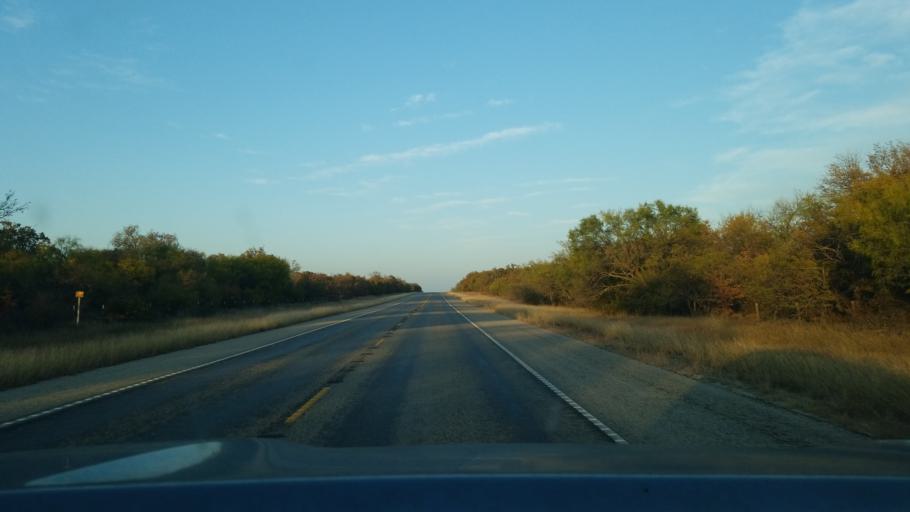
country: US
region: Texas
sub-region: Eastland County
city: Cisco
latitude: 32.4263
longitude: -98.9313
